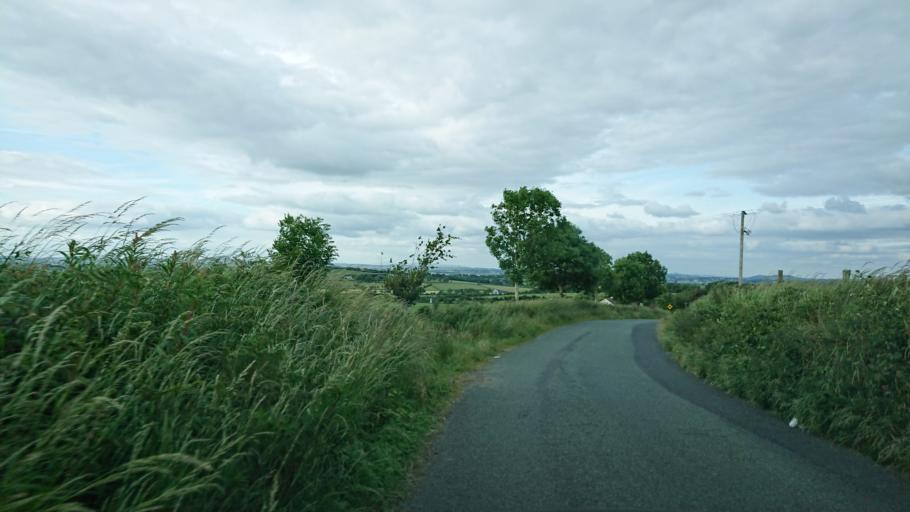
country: IE
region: Munster
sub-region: Waterford
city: Tra Mhor
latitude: 52.2125
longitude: -7.1982
